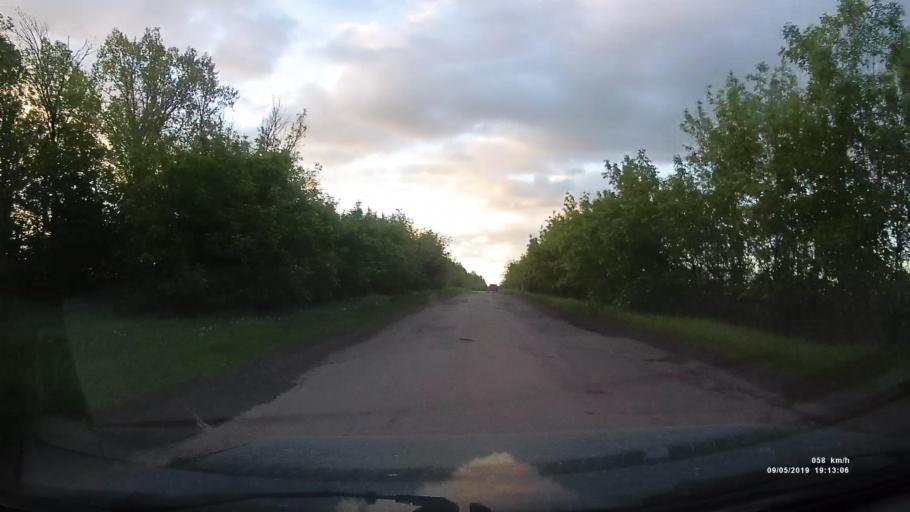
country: RU
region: Krasnodarskiy
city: Kanelovskaya
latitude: 46.7477
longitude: 39.2137
